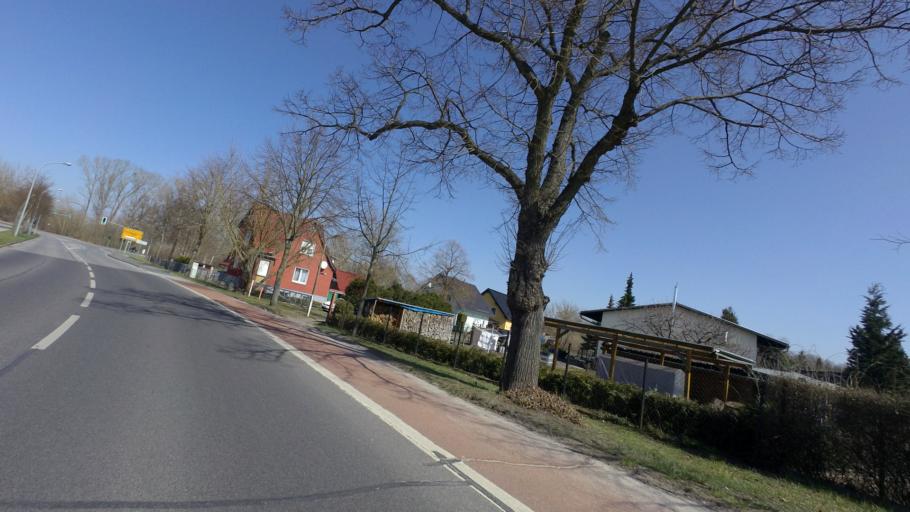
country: DE
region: Brandenburg
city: Oranienburg
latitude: 52.7725
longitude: 13.2473
